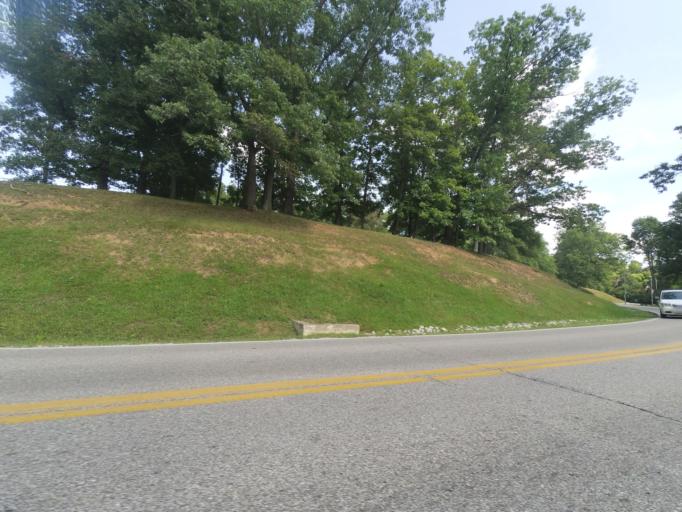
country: US
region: Ohio
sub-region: Lawrence County
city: Burlington
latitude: 38.3803
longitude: -82.5187
